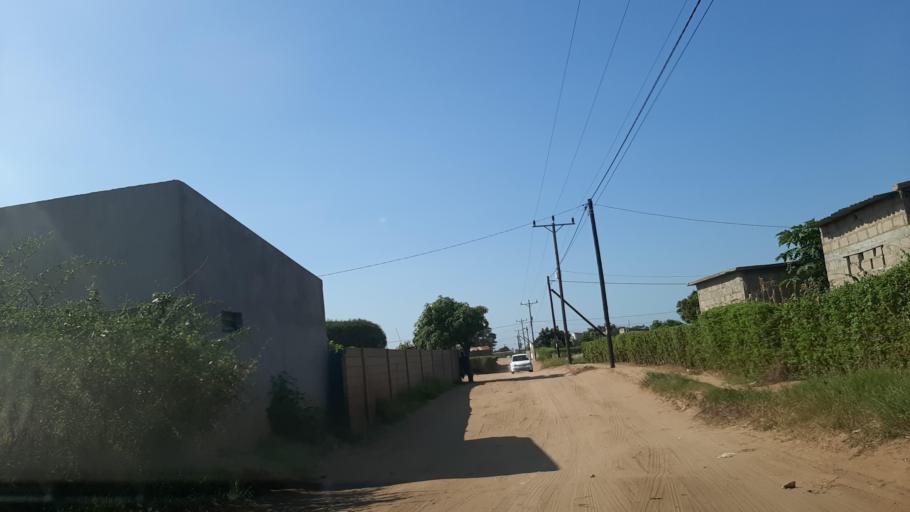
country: MZ
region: Maputo
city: Matola
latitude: -25.8023
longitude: 32.4910
